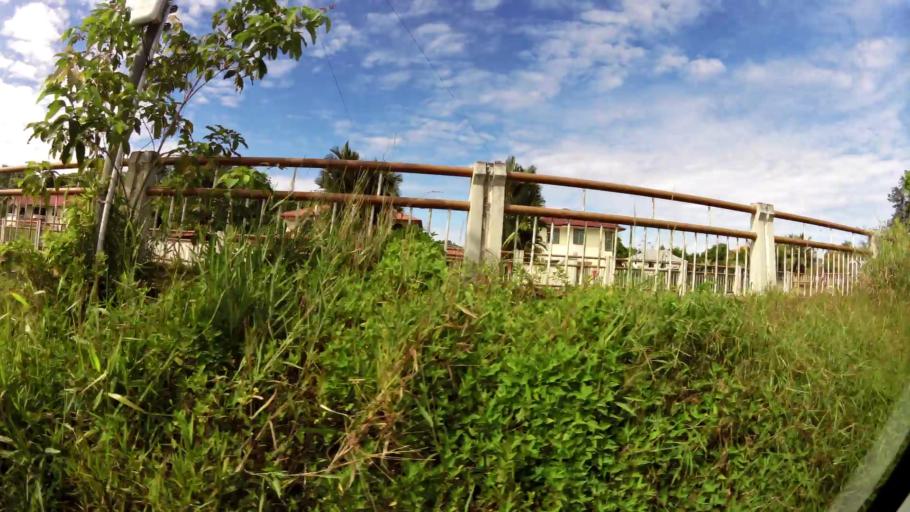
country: BN
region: Brunei and Muara
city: Bandar Seri Begawan
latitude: 4.9035
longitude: 114.9772
